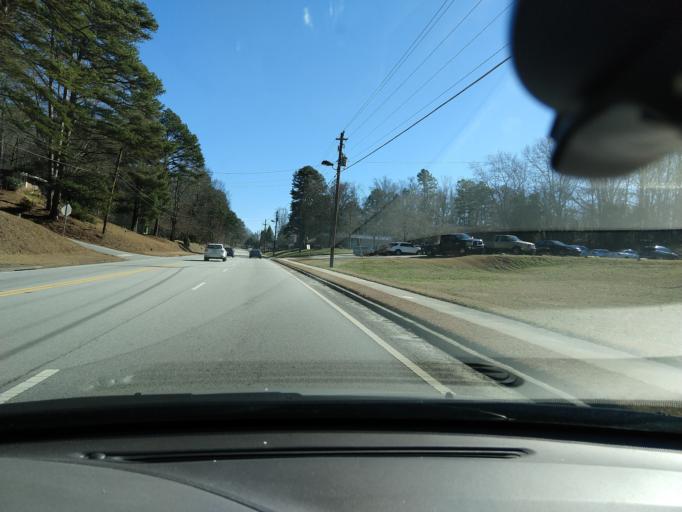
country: US
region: Georgia
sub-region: Stephens County
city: Toccoa
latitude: 34.5884
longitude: -83.3407
